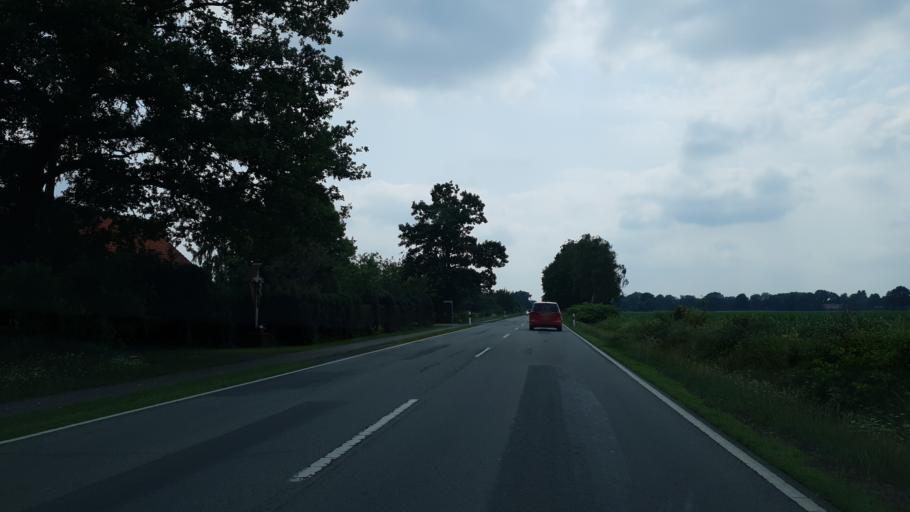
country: DE
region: Lower Saxony
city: Geeste
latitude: 52.5721
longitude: 7.2122
